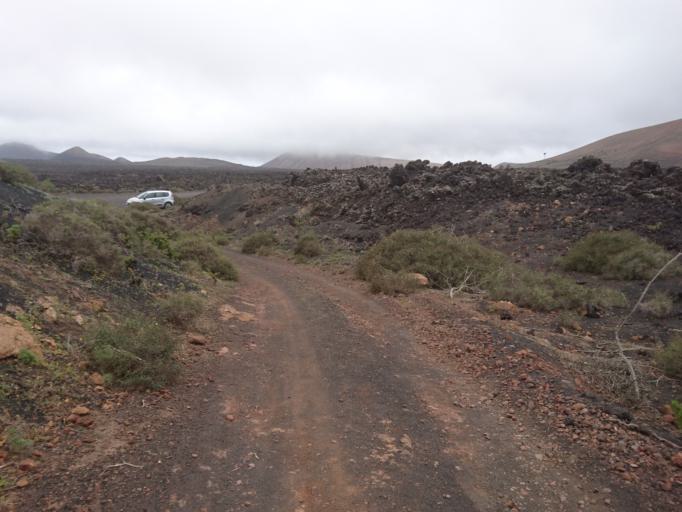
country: ES
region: Canary Islands
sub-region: Provincia de Las Palmas
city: Tinajo
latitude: 29.0171
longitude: -13.6944
